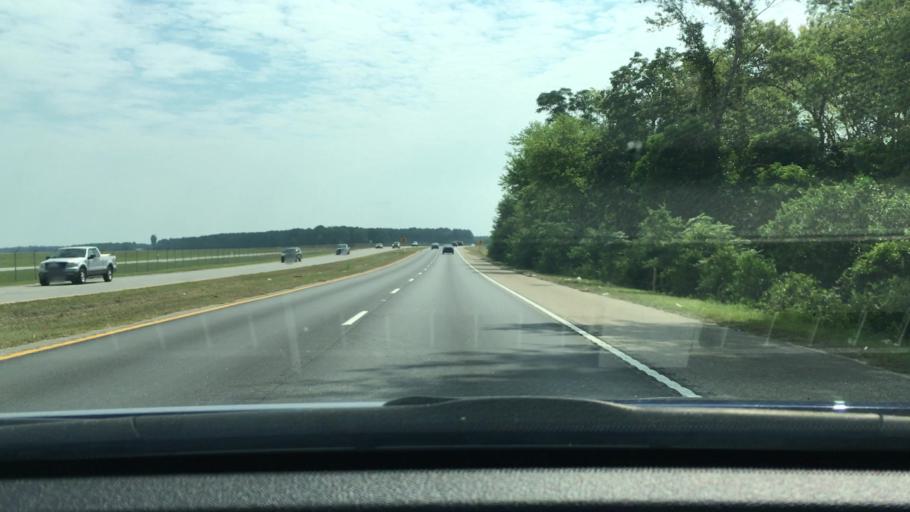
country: US
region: South Carolina
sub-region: Sumter County
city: Cherryvale
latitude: 33.9585
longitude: -80.4791
